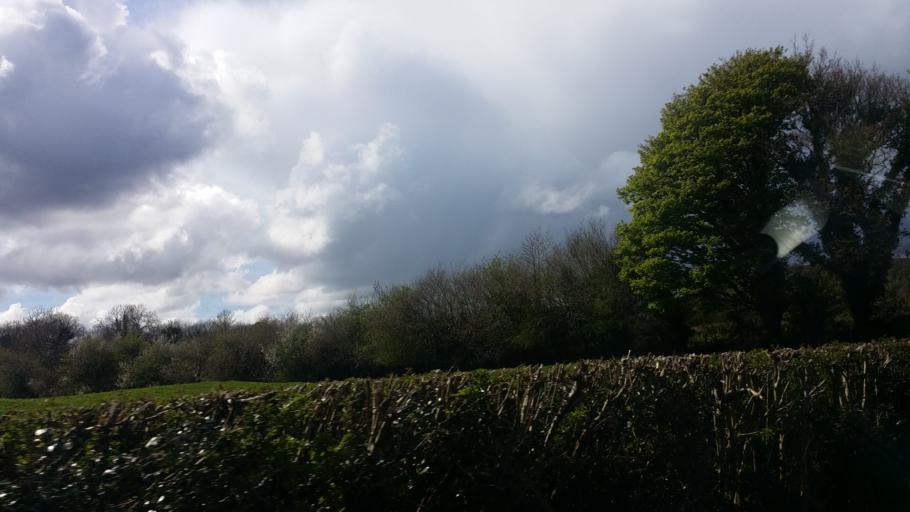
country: GB
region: Northern Ireland
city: Irvinestown
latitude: 54.4389
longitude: -7.7933
